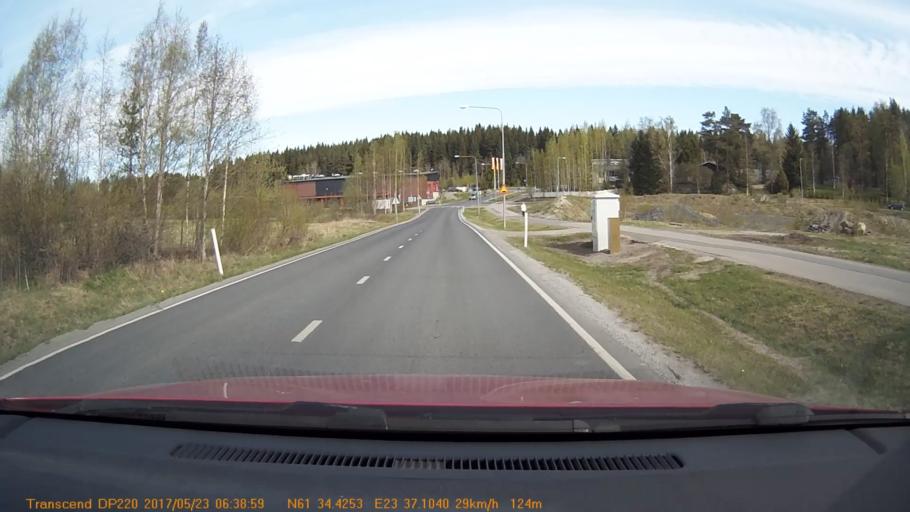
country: FI
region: Pirkanmaa
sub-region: Tampere
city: Yloejaervi
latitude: 61.5737
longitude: 23.6185
